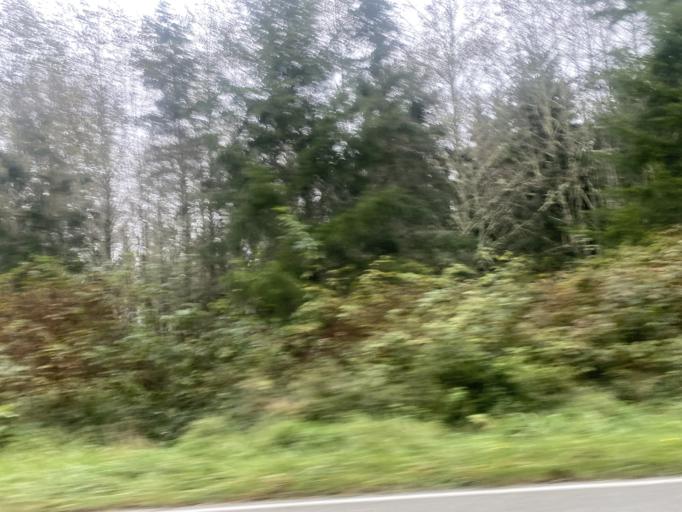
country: US
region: Washington
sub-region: Island County
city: Freeland
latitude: 48.0883
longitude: -122.5005
